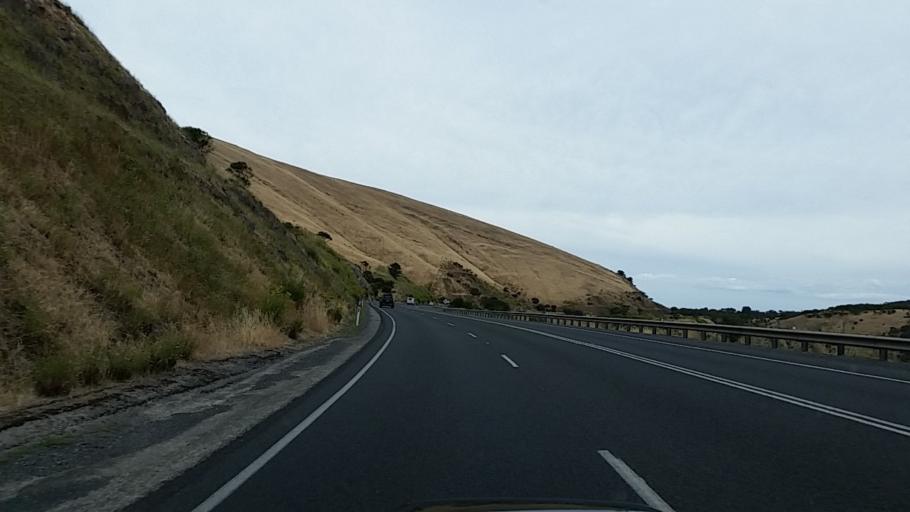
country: AU
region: South Australia
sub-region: Onkaparinga
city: Port Willunga
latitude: -35.3560
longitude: 138.4485
